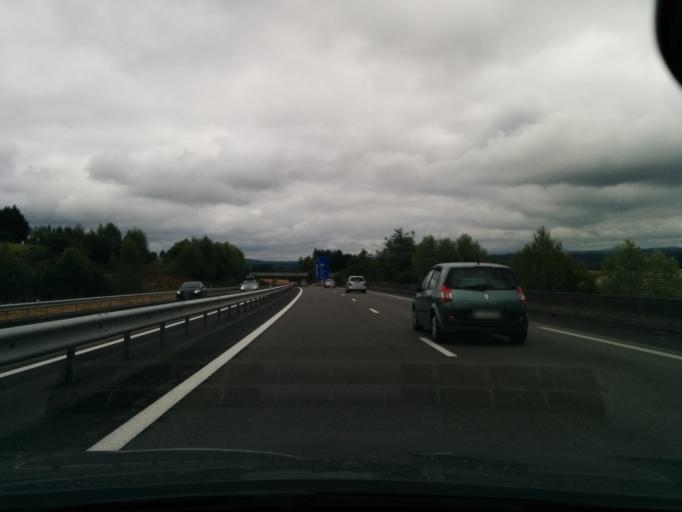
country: FR
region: Limousin
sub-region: Departement de la Correze
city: Sainte-Fereole
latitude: 45.2866
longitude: 1.5713
